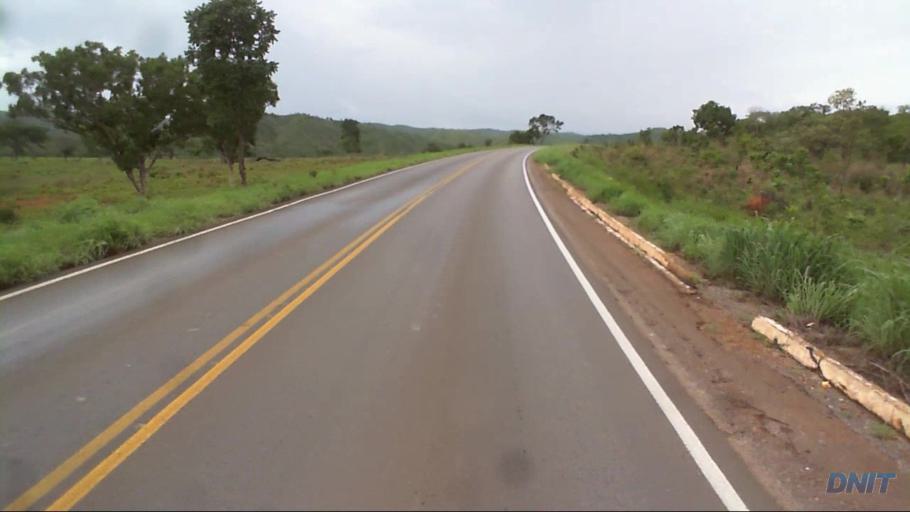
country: BR
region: Goias
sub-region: Padre Bernardo
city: Padre Bernardo
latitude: -15.4376
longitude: -48.1934
